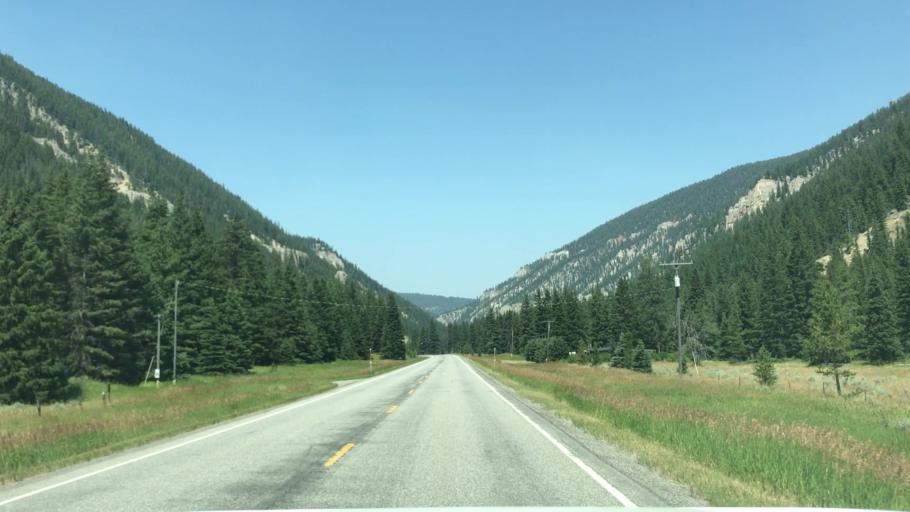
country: US
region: Montana
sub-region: Gallatin County
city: Big Sky
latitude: 45.1226
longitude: -111.2292
